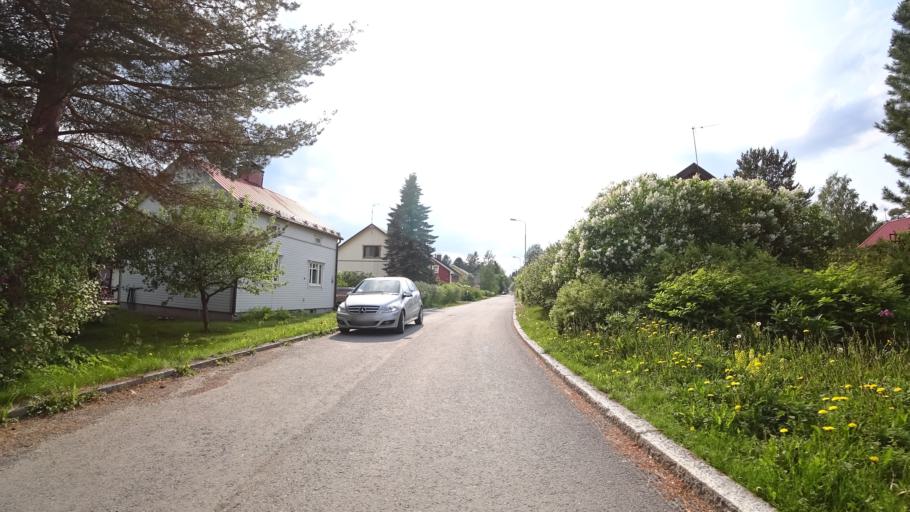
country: FI
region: Pirkanmaa
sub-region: Tampere
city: Pirkkala
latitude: 61.5037
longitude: 23.6277
